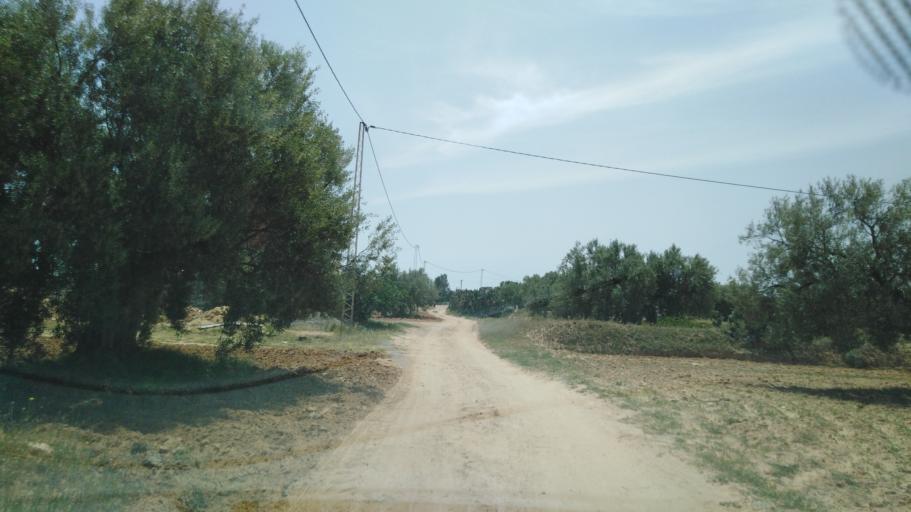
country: TN
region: Safaqis
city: Sfax
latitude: 34.7298
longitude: 10.5555
